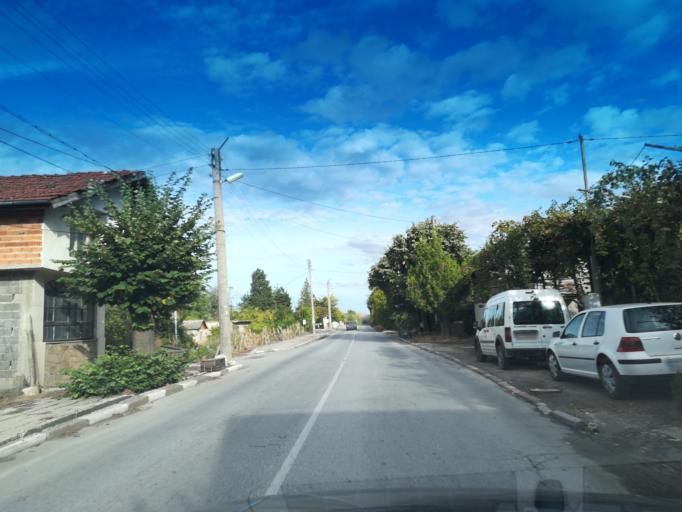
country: BG
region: Pazardzhik
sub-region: Obshtina Bratsigovo
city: Bratsigovo
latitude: 42.0674
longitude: 24.3835
